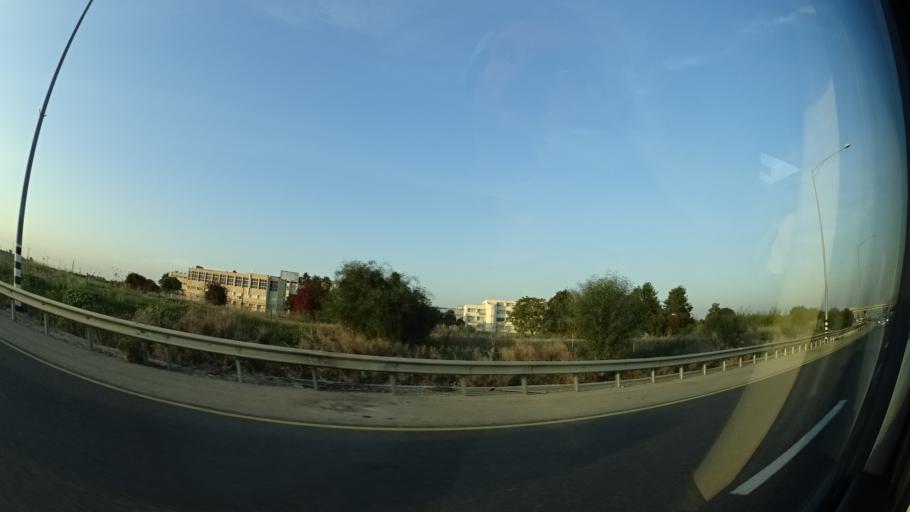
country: IL
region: Central District
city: Kefar Habad
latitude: 31.9913
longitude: 34.8659
